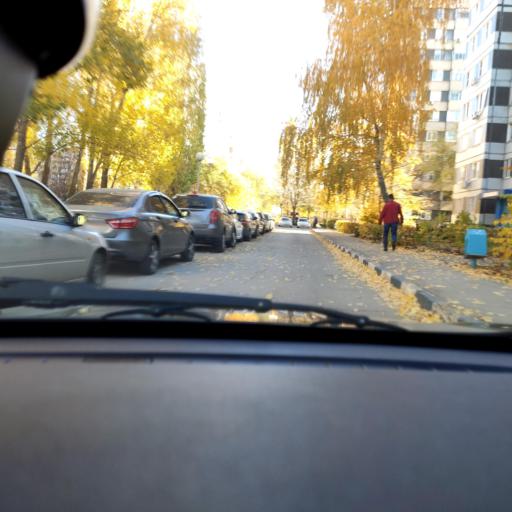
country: RU
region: Samara
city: Tol'yatti
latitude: 53.5216
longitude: 49.3156
